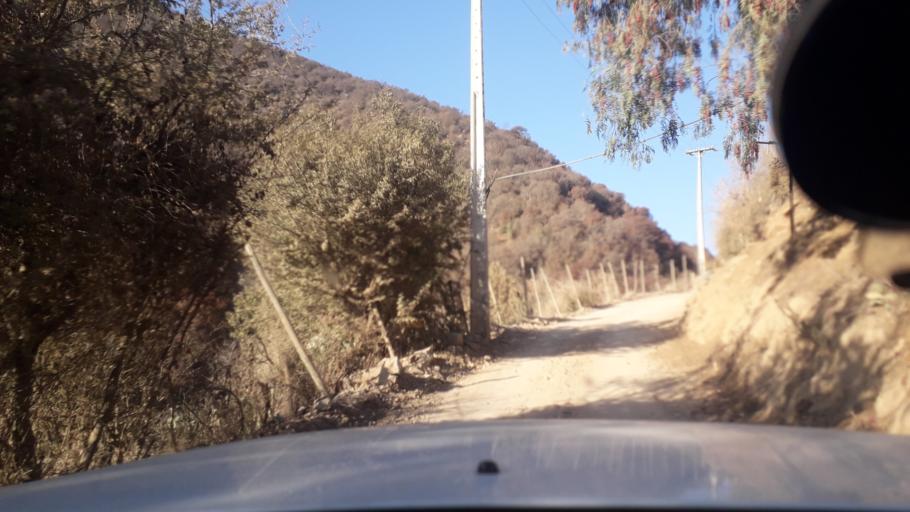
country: CL
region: Valparaiso
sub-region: Provincia de Marga Marga
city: Limache
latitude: -33.0517
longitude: -71.0765
